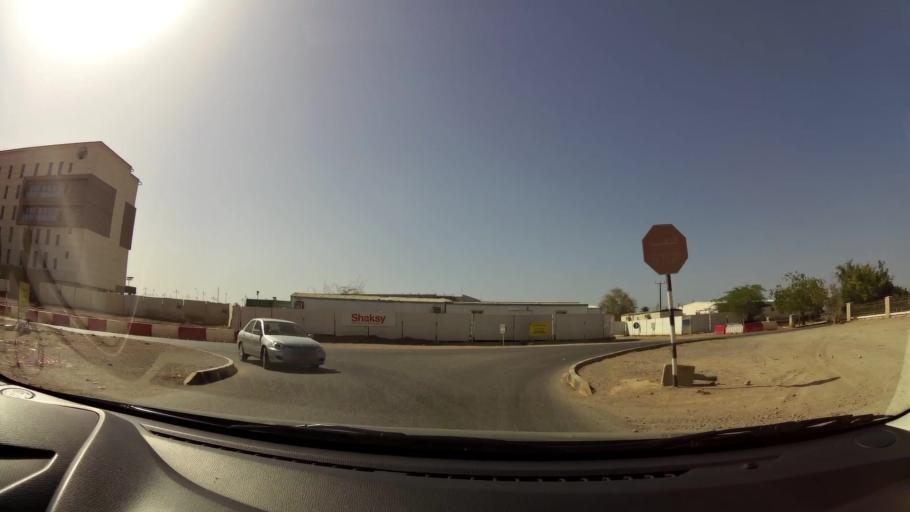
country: OM
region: Muhafazat Masqat
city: Bawshar
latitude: 23.5850
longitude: 58.3018
